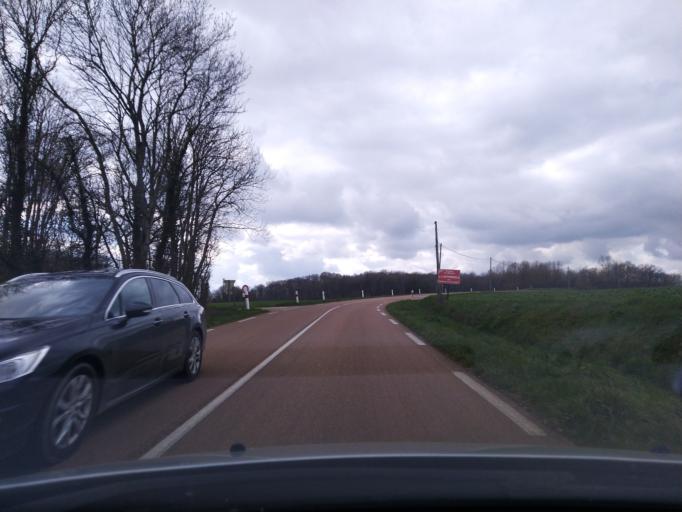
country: FR
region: Bourgogne
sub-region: Departement de l'Yonne
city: Avallon
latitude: 47.5260
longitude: 3.9920
